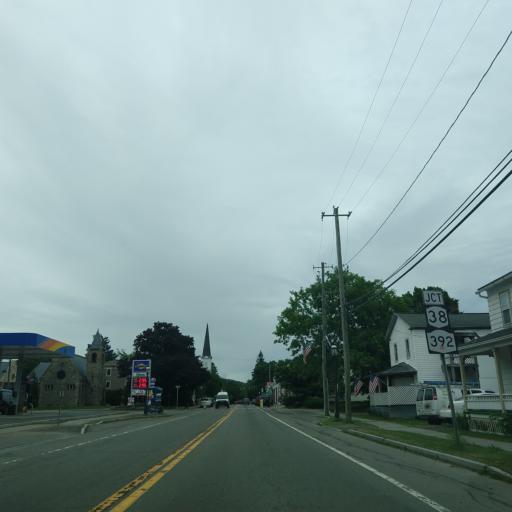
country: US
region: New York
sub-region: Tompkins County
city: Dryden
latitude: 42.4905
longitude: -76.3002
